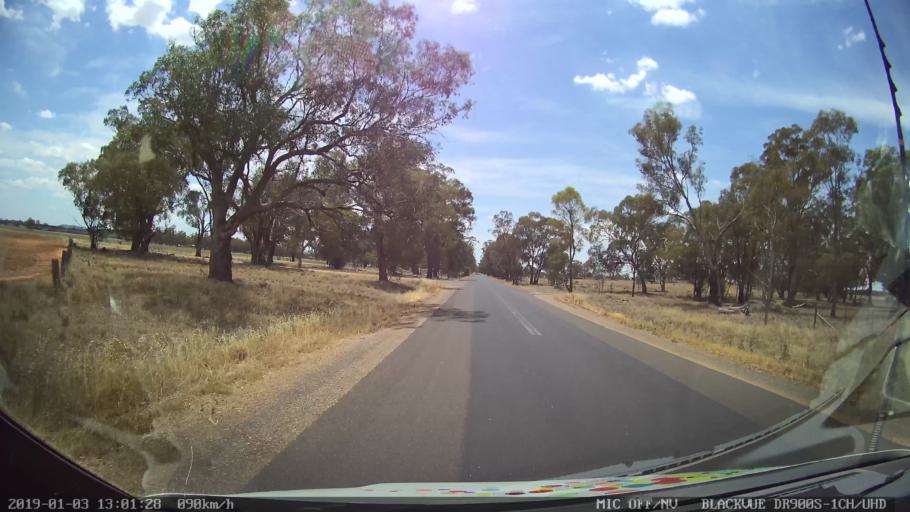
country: AU
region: New South Wales
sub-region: Cabonne
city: Canowindra
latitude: -33.6242
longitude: 148.4183
